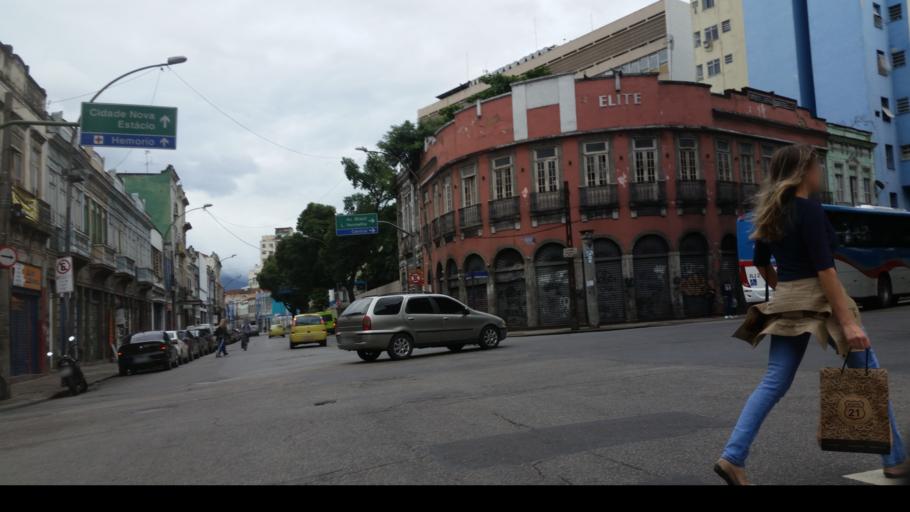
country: BR
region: Rio de Janeiro
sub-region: Rio De Janeiro
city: Rio de Janeiro
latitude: -22.9090
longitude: -43.1886
